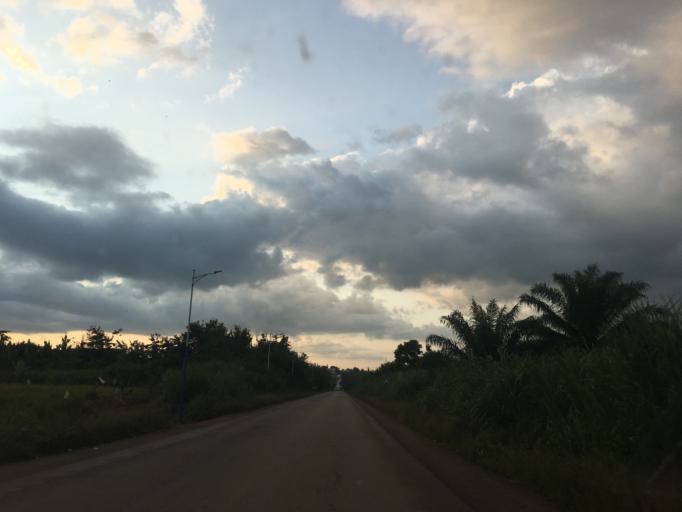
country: GH
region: Western
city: Bibiani
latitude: 6.7748
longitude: -2.5127
